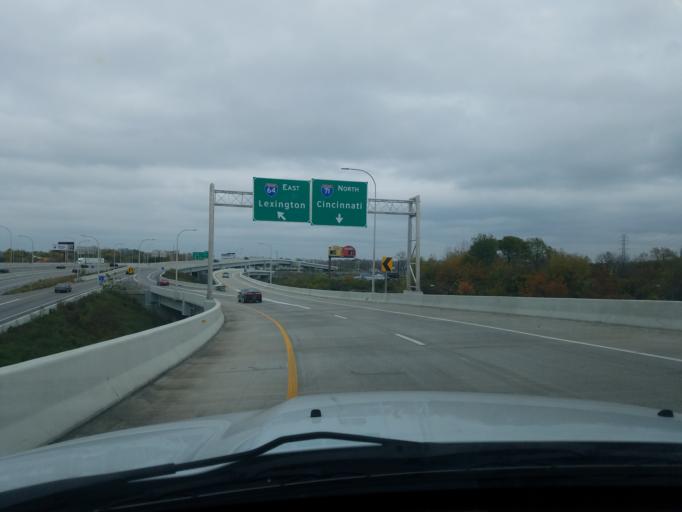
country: US
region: Indiana
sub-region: Clark County
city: Jeffersonville
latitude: 38.2584
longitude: -85.7390
